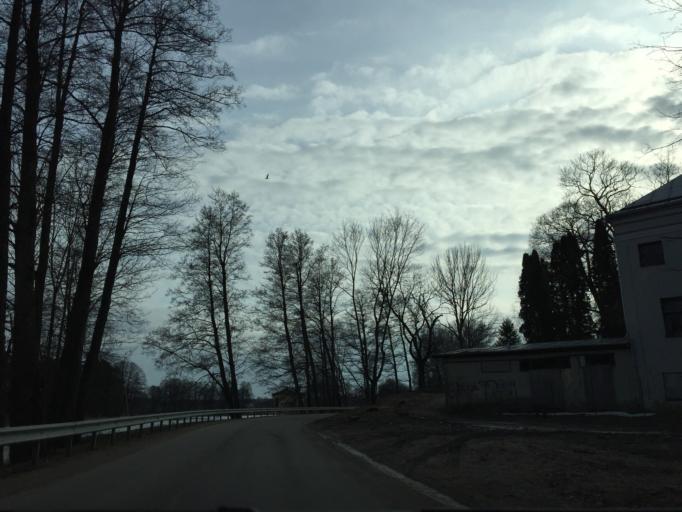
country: LV
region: Stopini
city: Ulbroka
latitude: 56.9399
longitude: 24.2859
